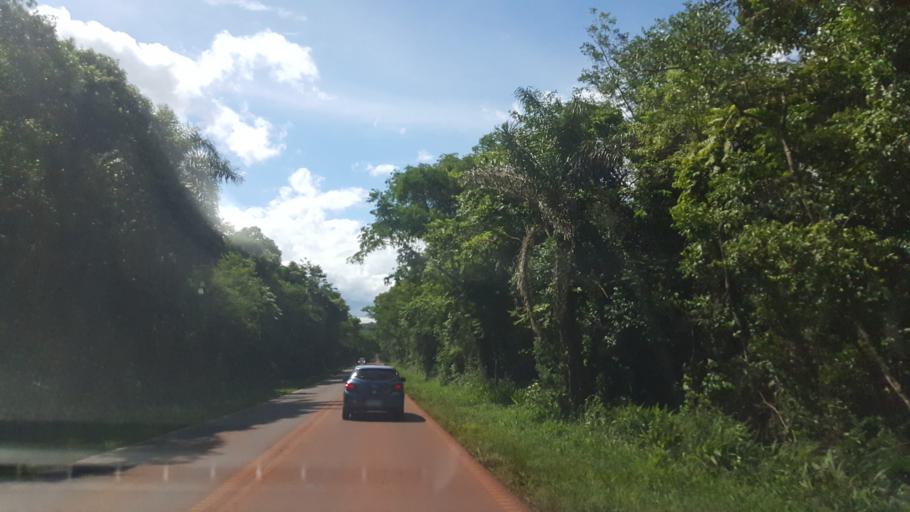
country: AR
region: Misiones
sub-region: Departamento de Iguazu
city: Puerto Iguazu
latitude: -25.7095
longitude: -54.4647
